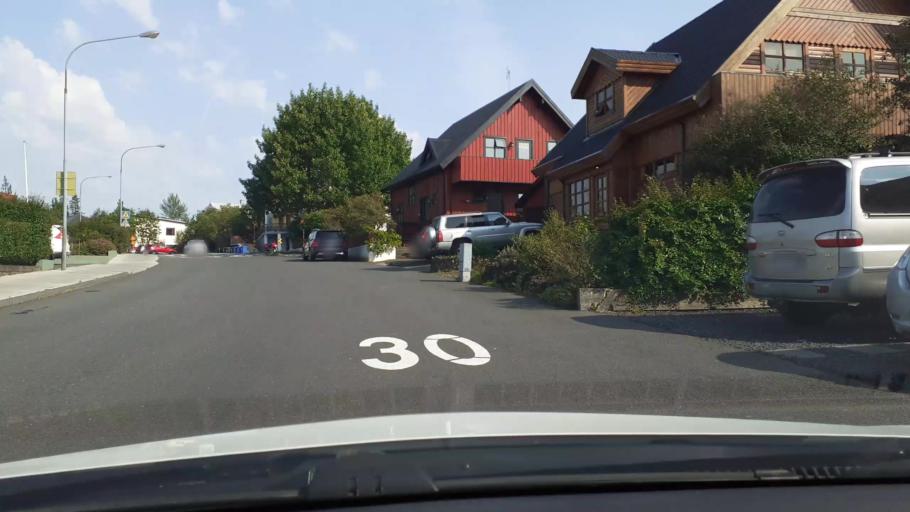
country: IS
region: Capital Region
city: Hafnarfjoerdur
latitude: 64.0733
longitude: -21.9606
